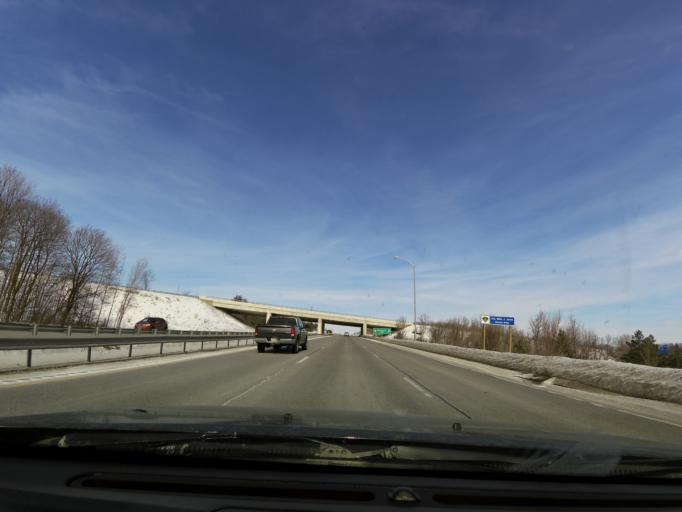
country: CA
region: Ontario
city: Orillia
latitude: 44.5879
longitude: -79.4458
